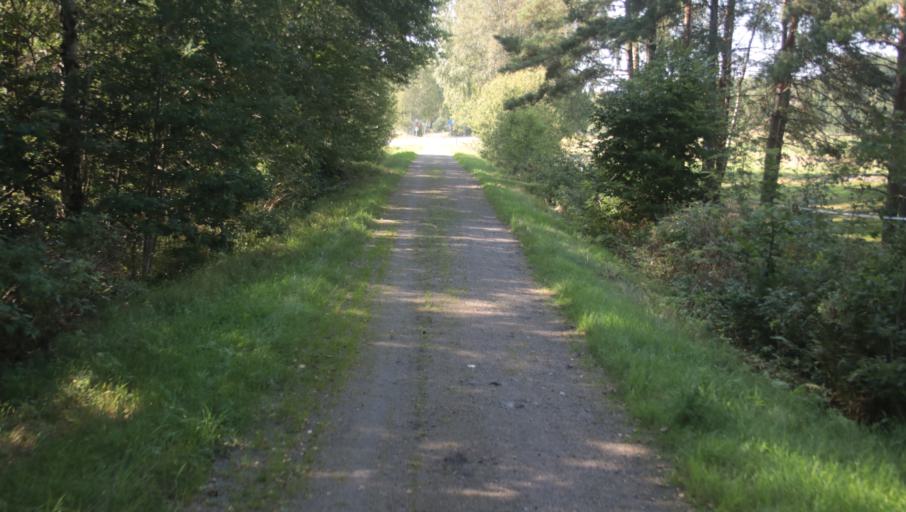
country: SE
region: Blekinge
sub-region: Karlshamns Kommun
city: Svangsta
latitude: 56.2970
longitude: 14.7376
